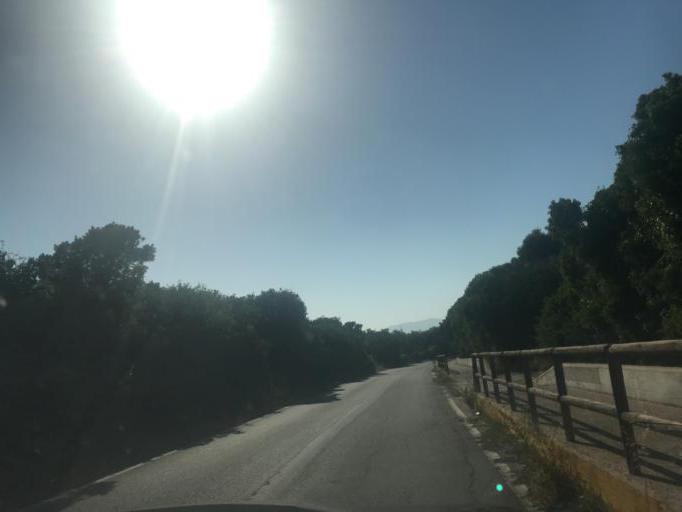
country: IT
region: Sardinia
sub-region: Provincia di Sassari
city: Alghero
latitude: 40.5541
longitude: 8.3342
